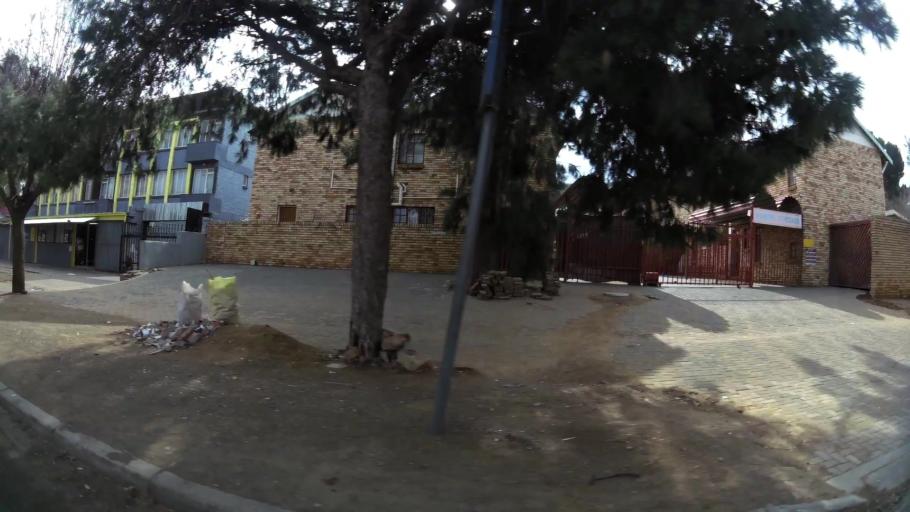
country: ZA
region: Orange Free State
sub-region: Mangaung Metropolitan Municipality
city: Bloemfontein
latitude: -29.1096
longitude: 26.2302
